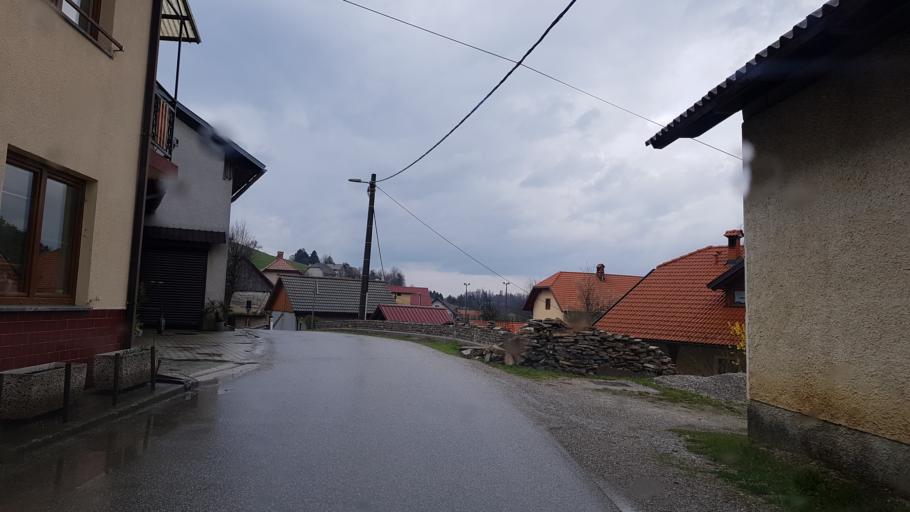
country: SI
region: Tolmin
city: Tolmin
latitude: 46.1382
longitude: 13.8200
